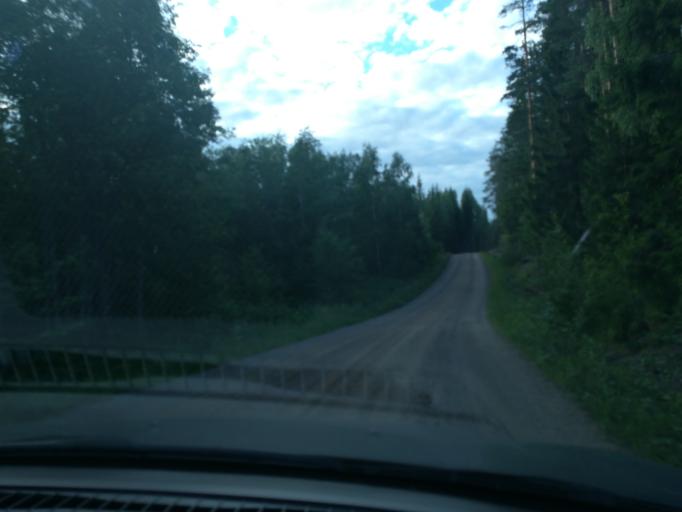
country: FI
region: Southern Savonia
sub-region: Mikkeli
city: Puumala
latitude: 61.6108
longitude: 28.1433
